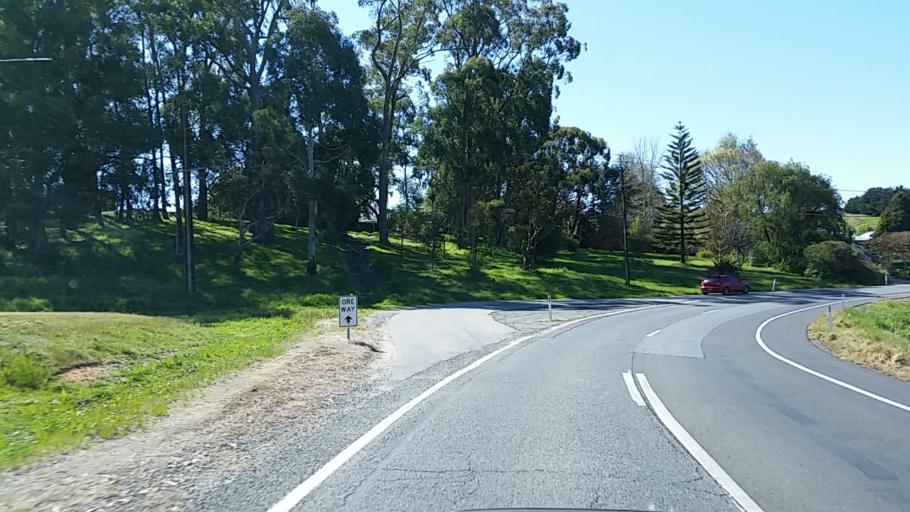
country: AU
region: South Australia
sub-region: Adelaide Hills
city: Bridgewater
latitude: -34.9732
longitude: 138.7303
